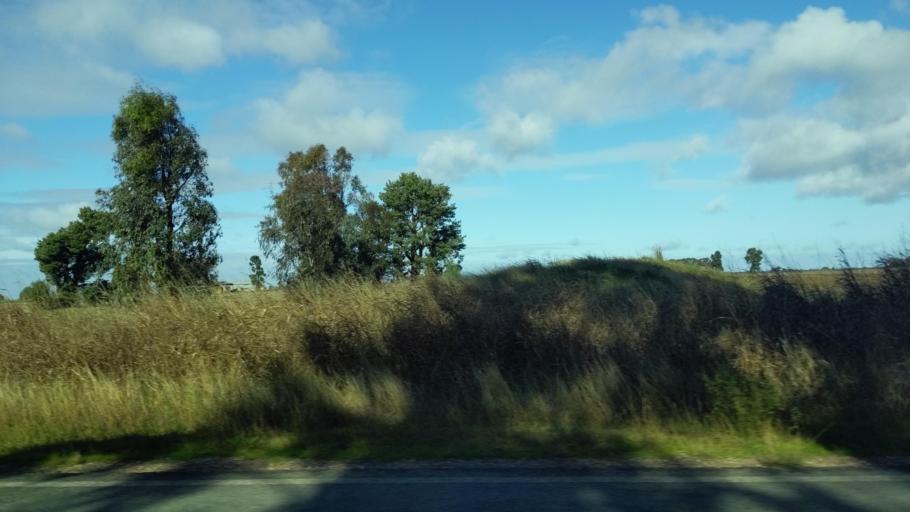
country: AU
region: New South Wales
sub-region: Narrandera
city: Narrandera
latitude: -34.7469
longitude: 146.8179
